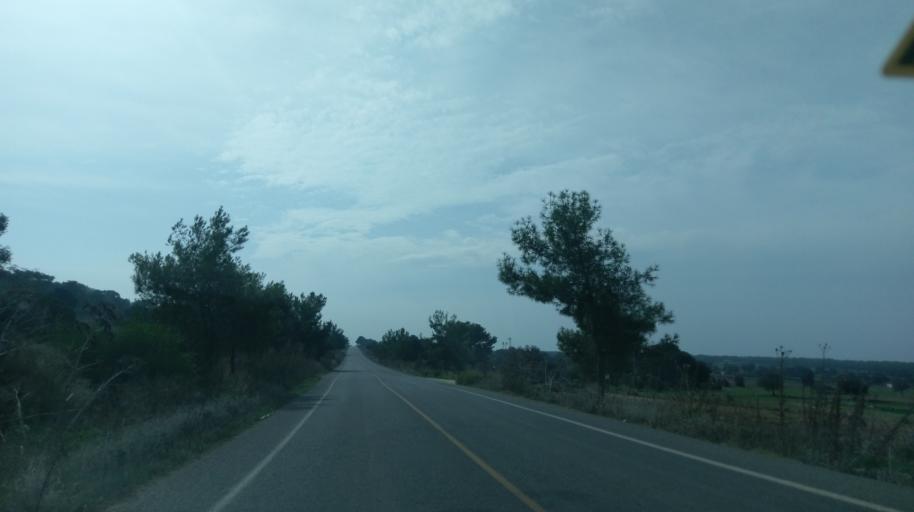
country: CY
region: Lefkosia
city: Morfou
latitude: 35.3113
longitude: 33.0488
